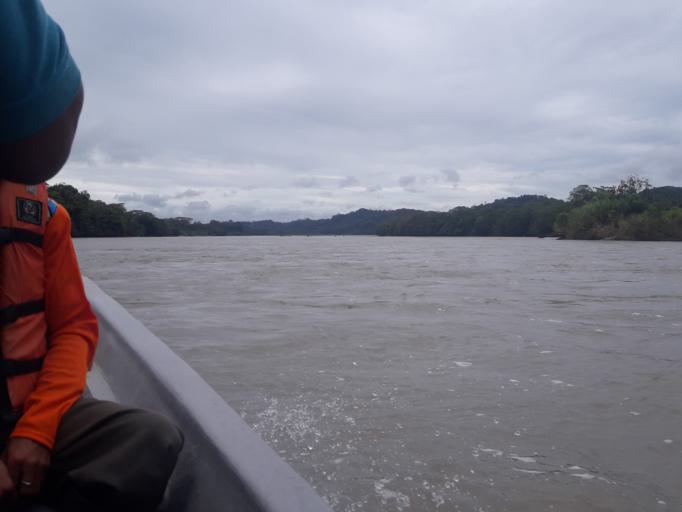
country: EC
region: Orellana
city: Boca Suno
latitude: -0.8817
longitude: -77.2971
